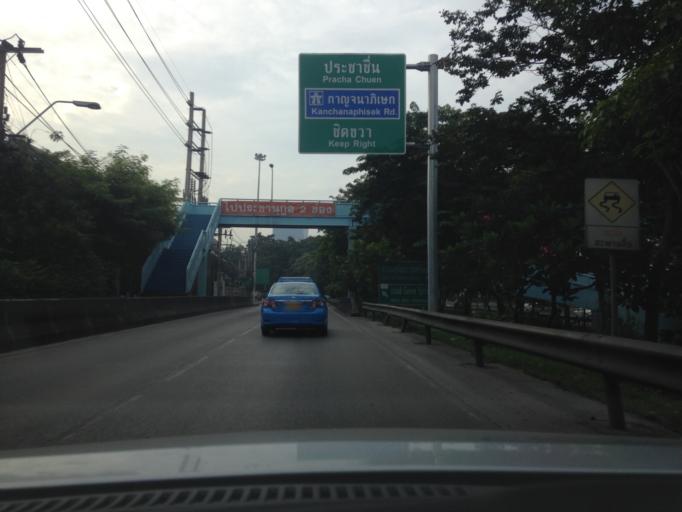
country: TH
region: Bangkok
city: Chatuchak
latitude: 13.8339
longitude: 100.5577
